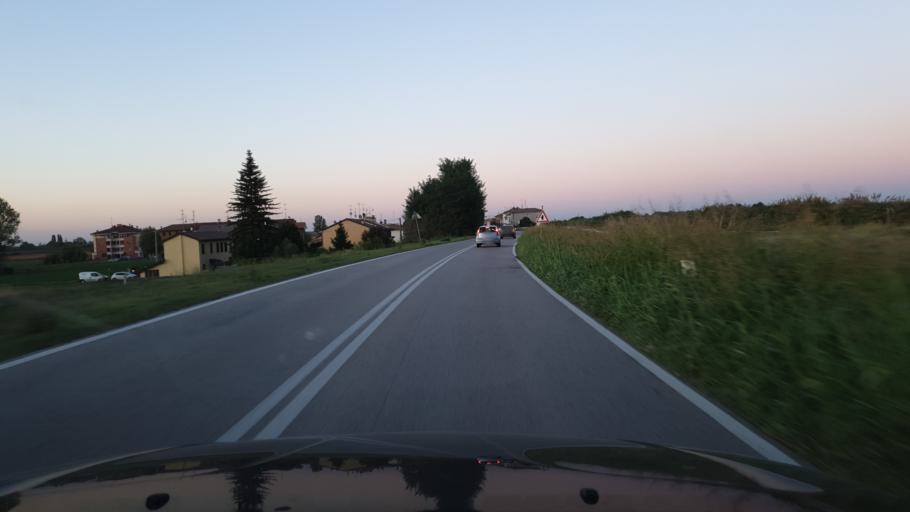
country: IT
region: Emilia-Romagna
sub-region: Provincia di Bologna
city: Ca De Fabbri
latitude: 44.6252
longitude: 11.4585
